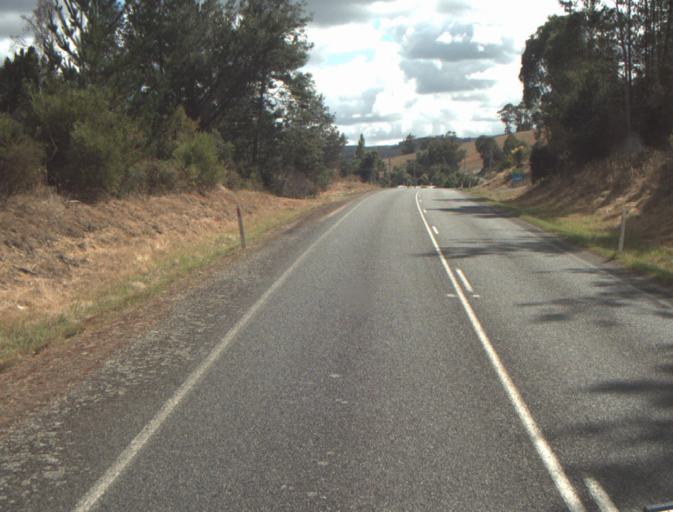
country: AU
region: Tasmania
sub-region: Launceston
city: Mayfield
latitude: -41.2648
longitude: 147.2158
